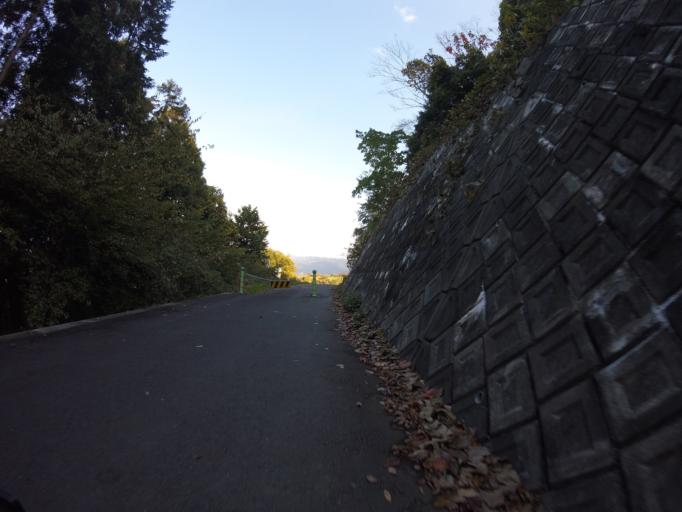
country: JP
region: Shizuoka
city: Mishima
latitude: 35.0818
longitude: 138.9068
